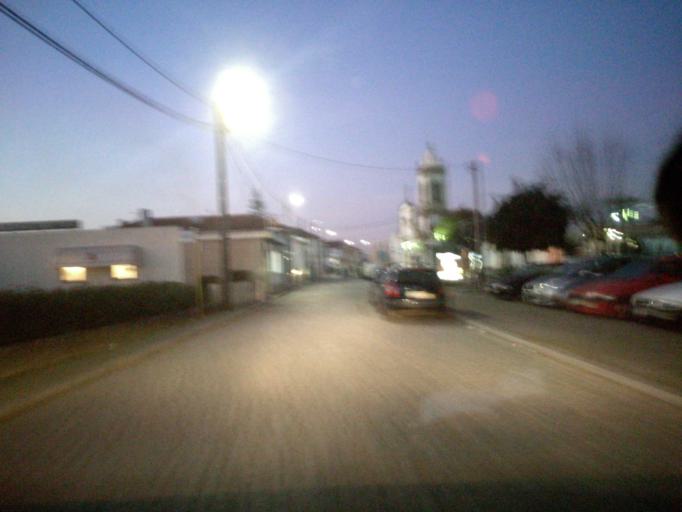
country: PT
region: Porto
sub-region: Maia
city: Nogueira
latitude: 41.2385
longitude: -8.5872
